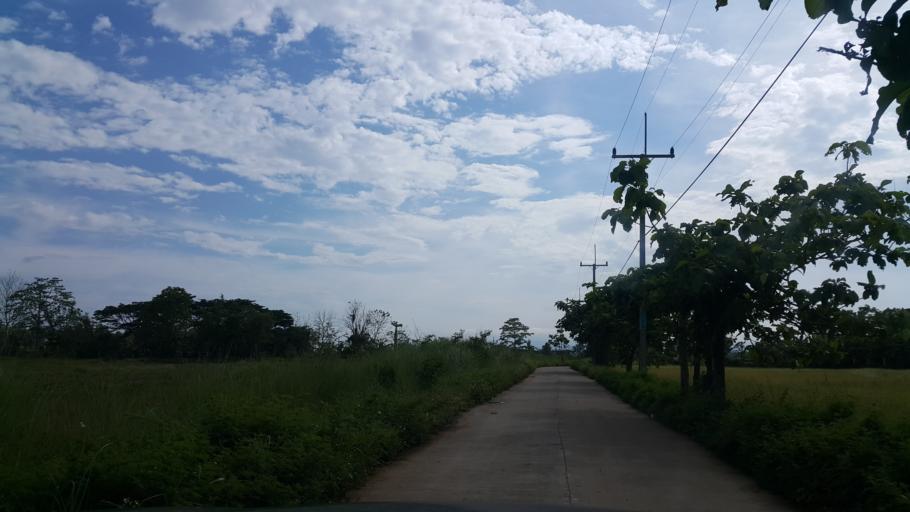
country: TH
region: Chiang Rai
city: Chiang Rai
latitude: 19.9719
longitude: 99.8986
